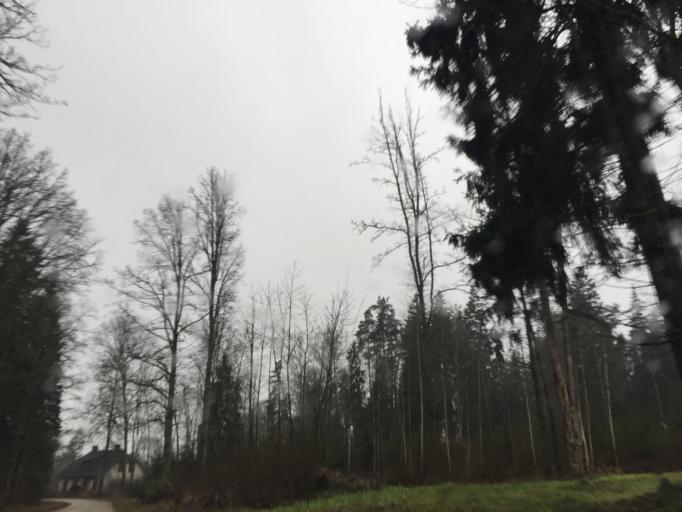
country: LV
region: Viesite
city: Viesite
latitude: 56.4628
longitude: 25.6271
